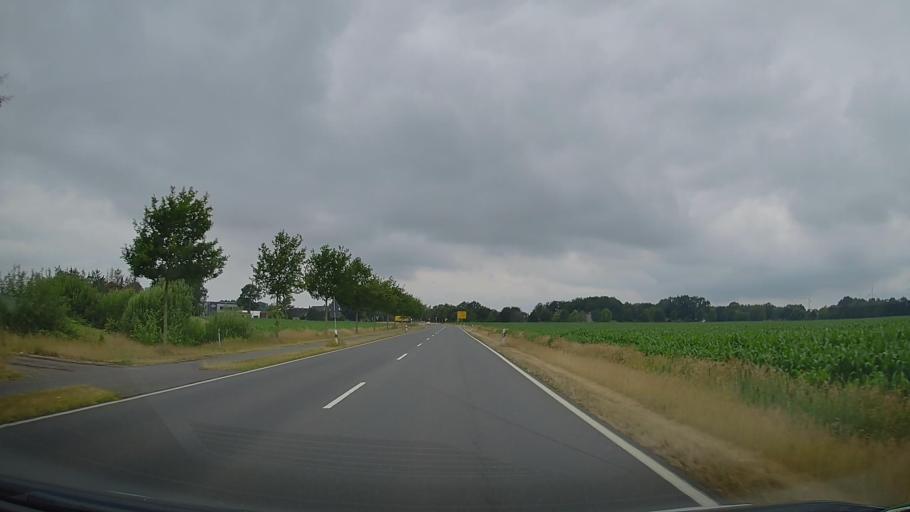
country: DE
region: Lower Saxony
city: Dinklage
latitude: 52.6784
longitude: 8.1325
